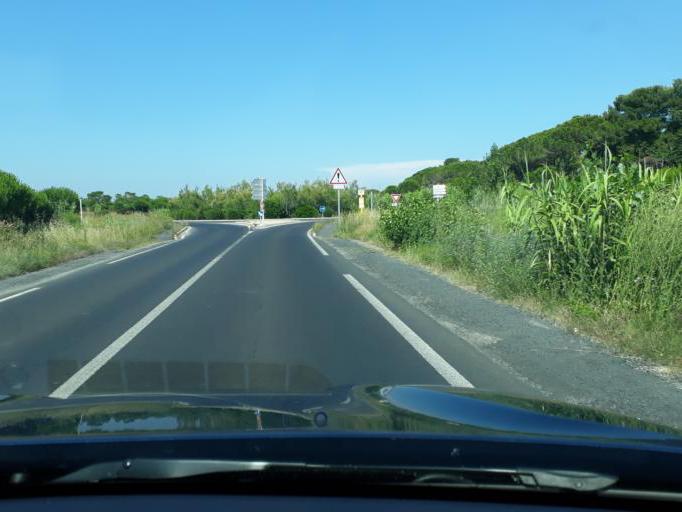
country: FR
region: Languedoc-Roussillon
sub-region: Departement de l'Herault
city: Marseillan
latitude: 43.3401
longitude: 3.5755
